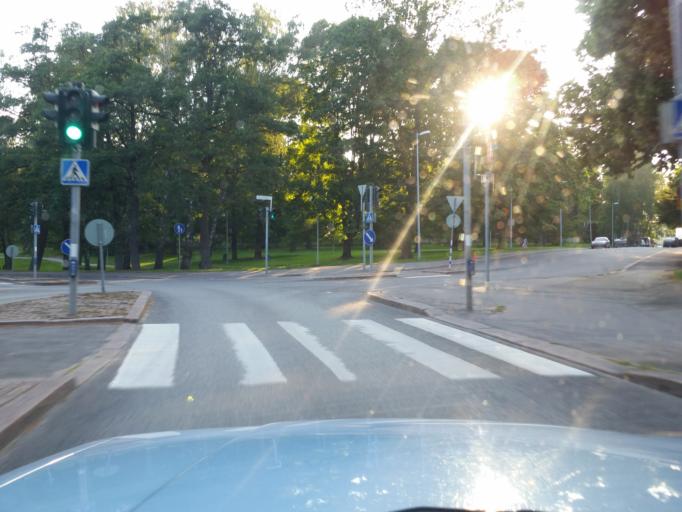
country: FI
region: Uusimaa
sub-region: Helsinki
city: Teekkarikylae
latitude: 60.1925
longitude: 24.8795
